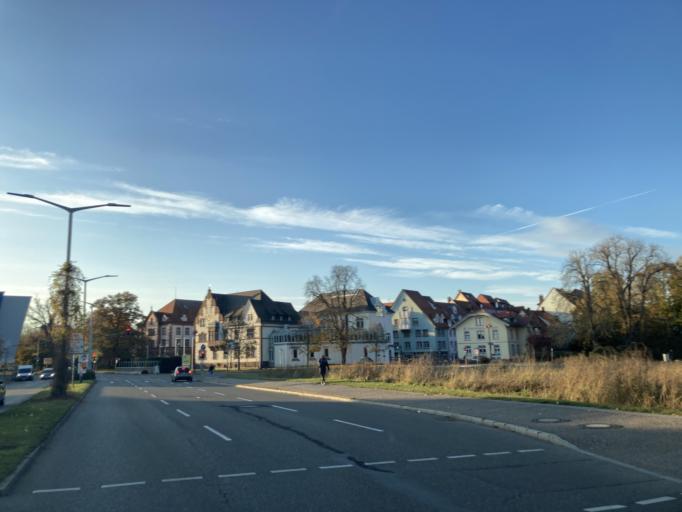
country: DE
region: Baden-Wuerttemberg
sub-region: Freiburg Region
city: Villingen-Schwenningen
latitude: 48.0553
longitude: 8.4633
